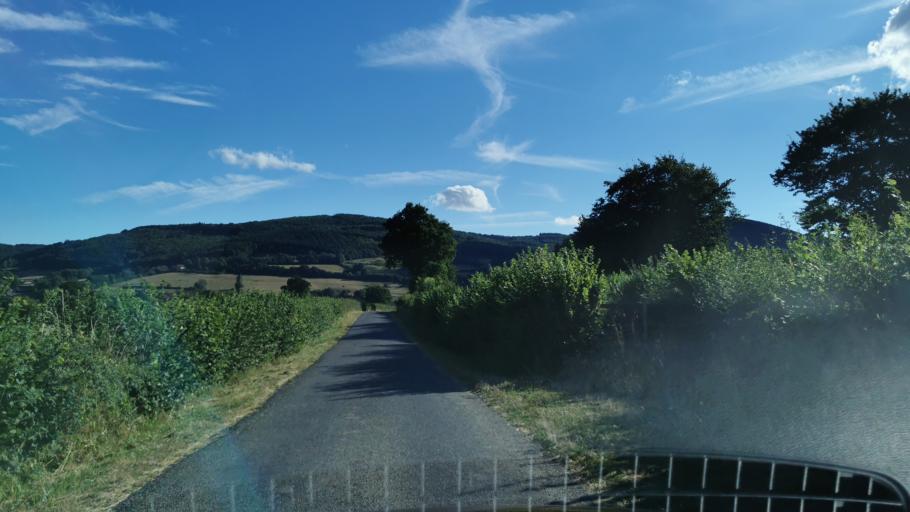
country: FR
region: Bourgogne
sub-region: Departement de Saone-et-Loire
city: Marmagne
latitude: 46.8640
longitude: 4.3127
